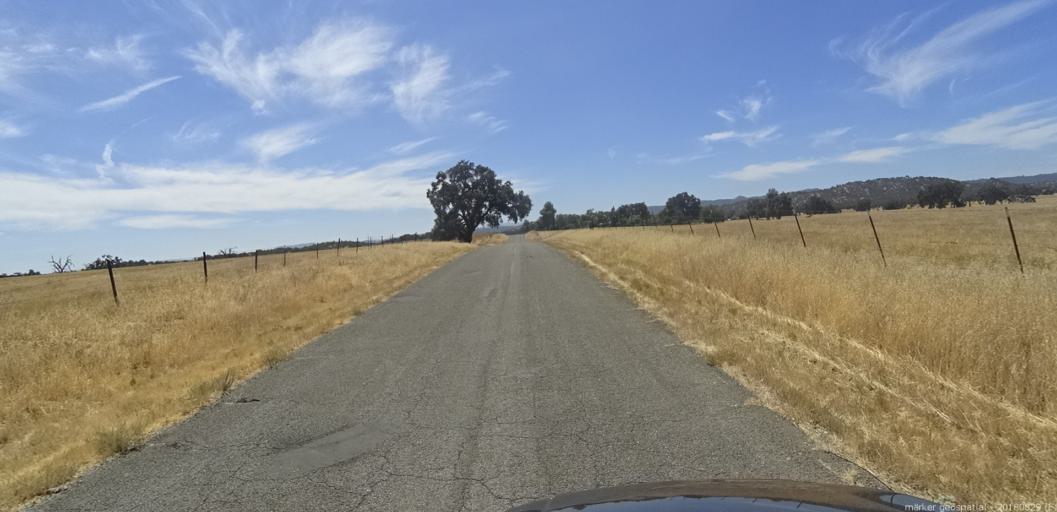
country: US
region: California
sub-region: San Luis Obispo County
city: Lake Nacimiento
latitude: 35.9281
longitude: -121.0643
